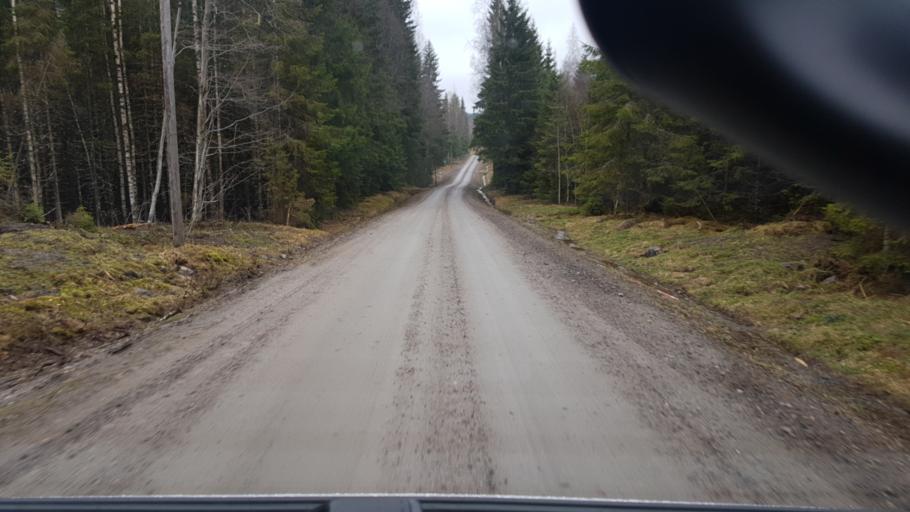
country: SE
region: Vaermland
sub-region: Eda Kommun
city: Charlottenberg
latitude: 59.9879
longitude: 12.4820
